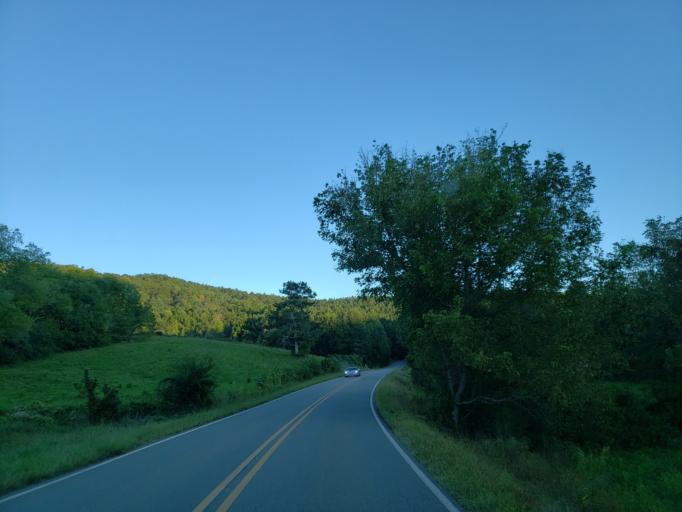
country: US
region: Georgia
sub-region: Bartow County
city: Rydal
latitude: 34.3680
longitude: -84.5810
